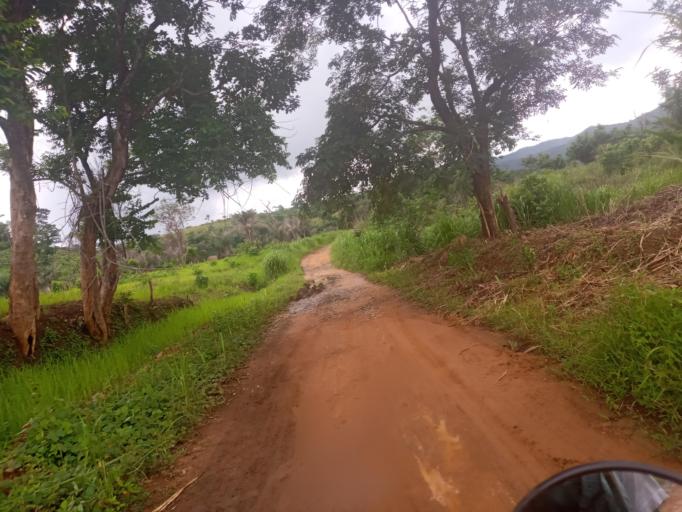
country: SL
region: Northern Province
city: Bumbuna
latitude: 8.9269
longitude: -11.7441
